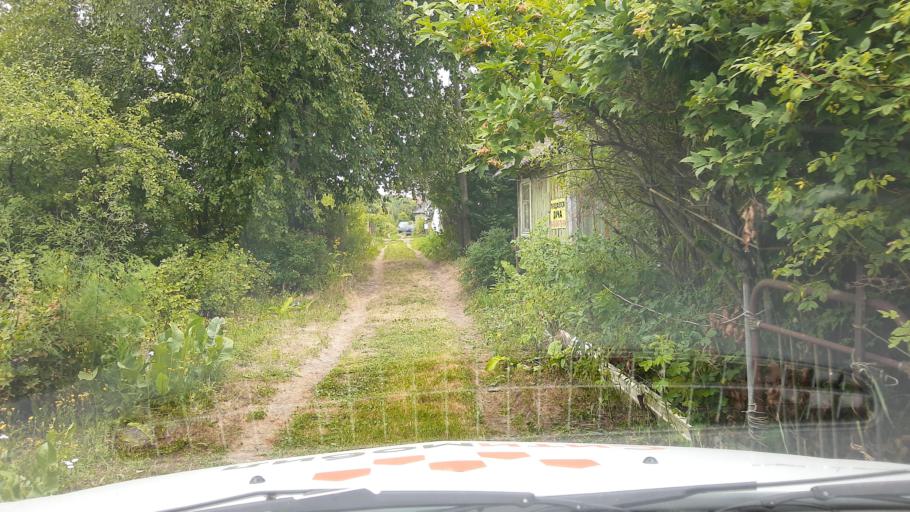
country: RU
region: Bashkortostan
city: Ufa
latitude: 54.8037
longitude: 56.1546
